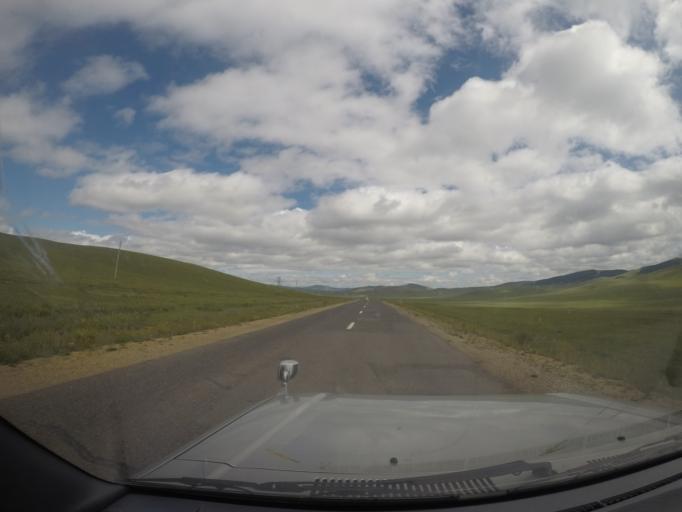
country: MN
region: Hentiy
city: Modot
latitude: 47.7729
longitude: 108.8591
